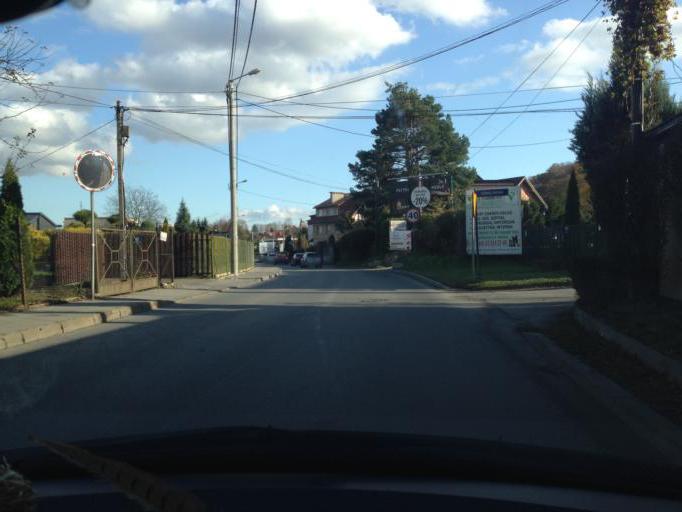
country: PL
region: Lesser Poland Voivodeship
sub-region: Powiat krakowski
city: Rzaska
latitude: 50.0679
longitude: 19.8484
